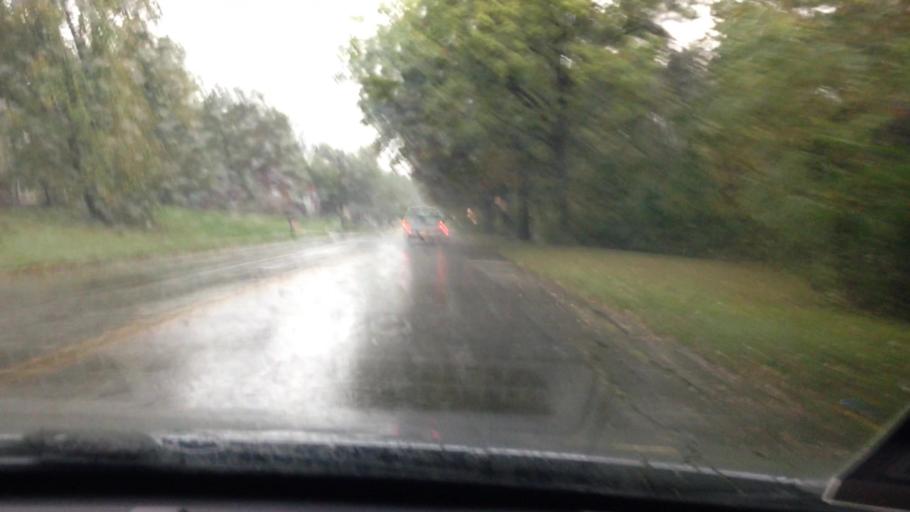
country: US
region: Kansas
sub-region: Leavenworth County
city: Leavenworth
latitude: 39.3041
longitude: -94.9275
